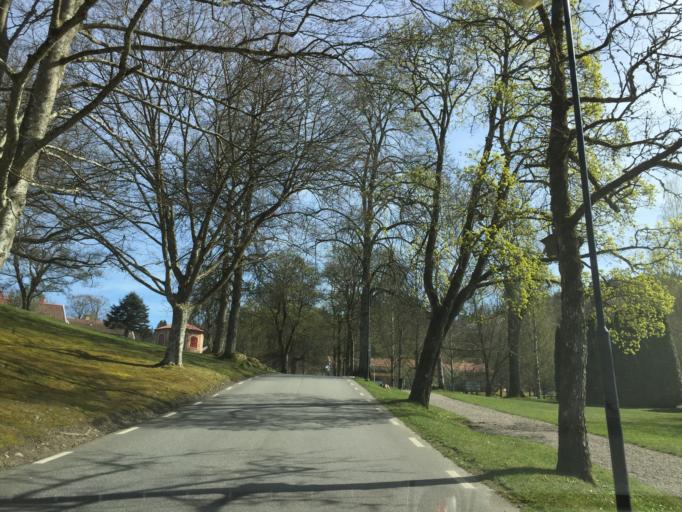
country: SE
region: Vaestra Goetaland
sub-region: Uddevalla Kommun
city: Uddevalla
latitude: 58.3296
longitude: 11.9037
